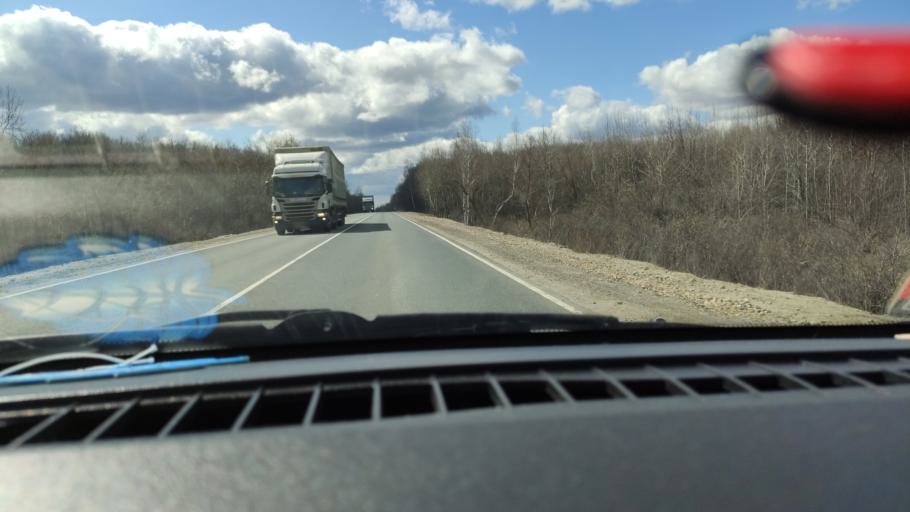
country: RU
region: Saratov
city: Khvalynsk
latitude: 52.4493
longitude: 48.0113
